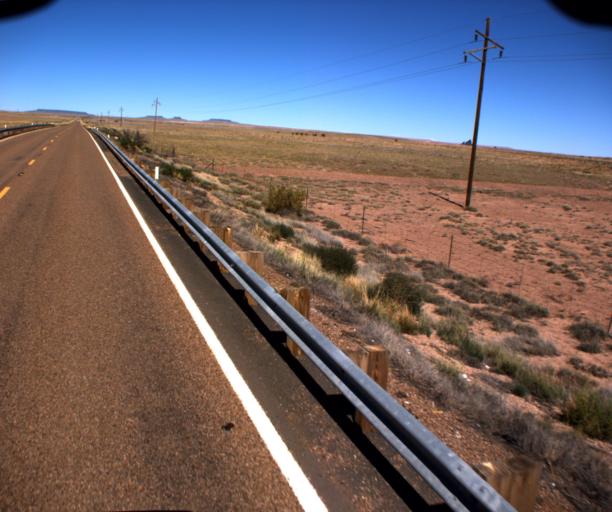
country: US
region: Arizona
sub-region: Navajo County
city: Holbrook
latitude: 35.0869
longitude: -110.0978
